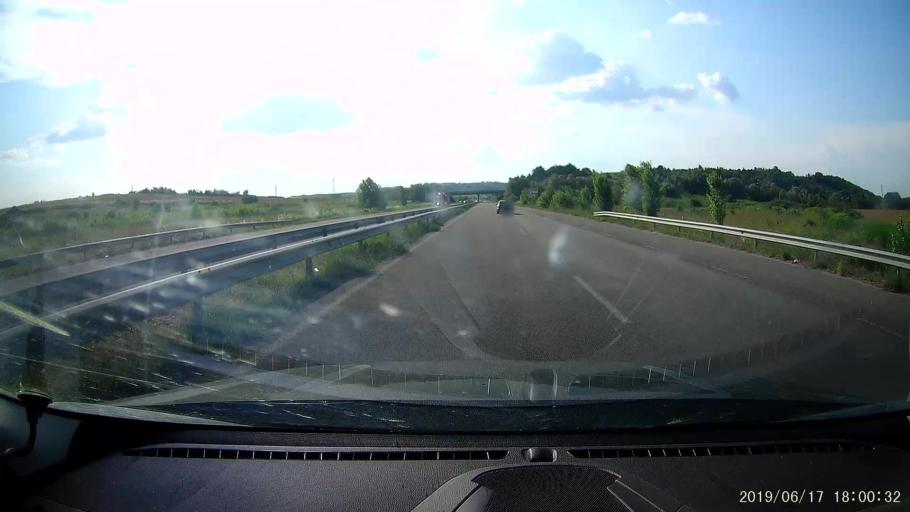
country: BG
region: Khaskovo
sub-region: Obshtina Svilengrad
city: Svilengrad
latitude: 41.7375
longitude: 26.2775
